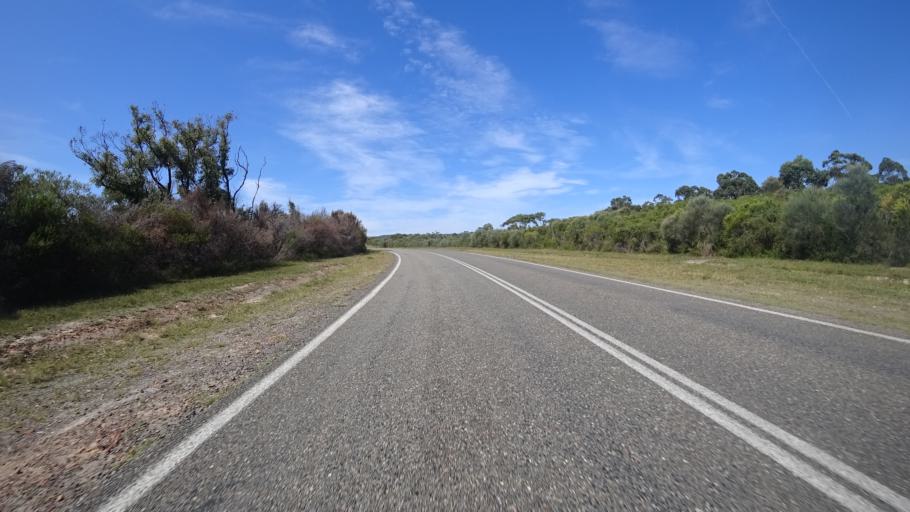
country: AU
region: New South Wales
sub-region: Shoalhaven Shire
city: Falls Creek
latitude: -35.1436
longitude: 150.7048
